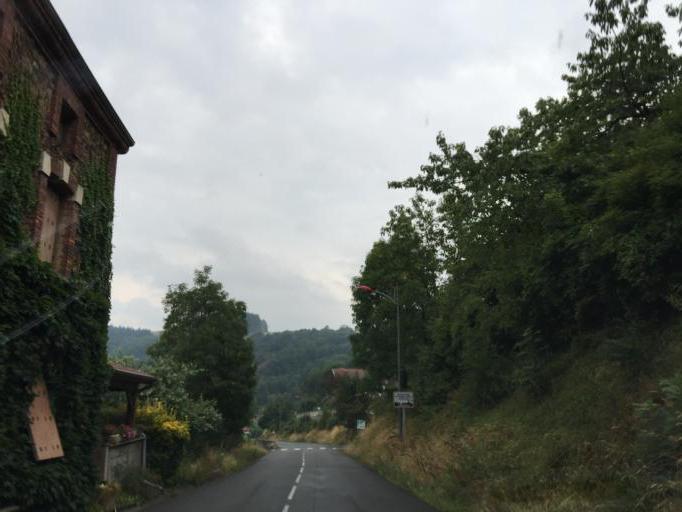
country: FR
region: Rhone-Alpes
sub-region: Departement de la Loire
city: Saint-Christo-en-Jarez
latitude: 45.5249
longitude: 4.4914
